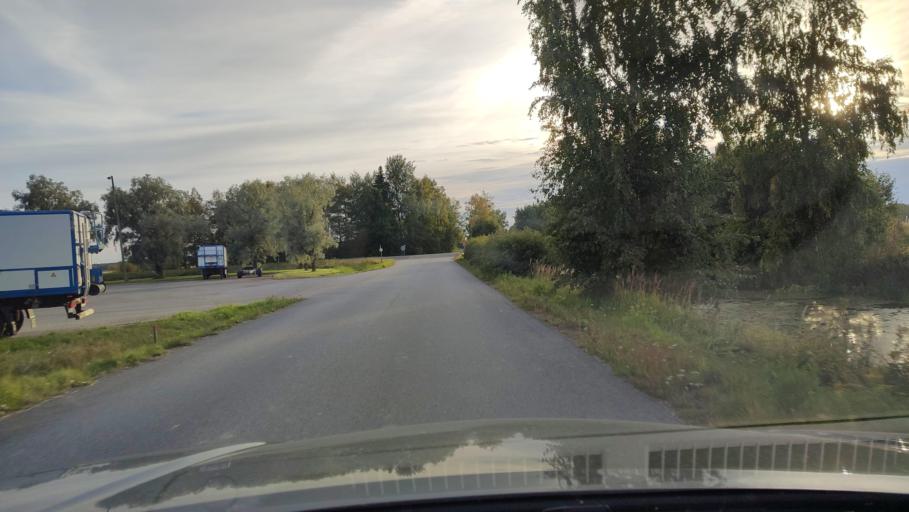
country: FI
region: Ostrobothnia
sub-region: Sydosterbotten
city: Kristinestad
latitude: 62.2458
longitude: 21.5026
